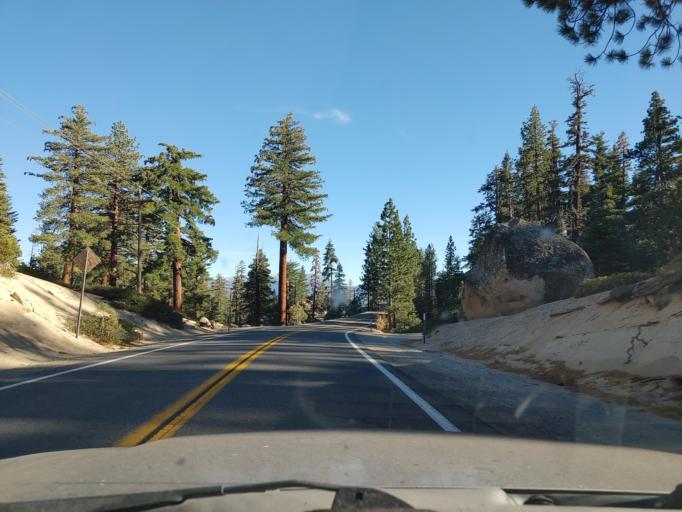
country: US
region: California
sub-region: Placer County
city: Tahoma
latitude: 38.9769
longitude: -120.1018
